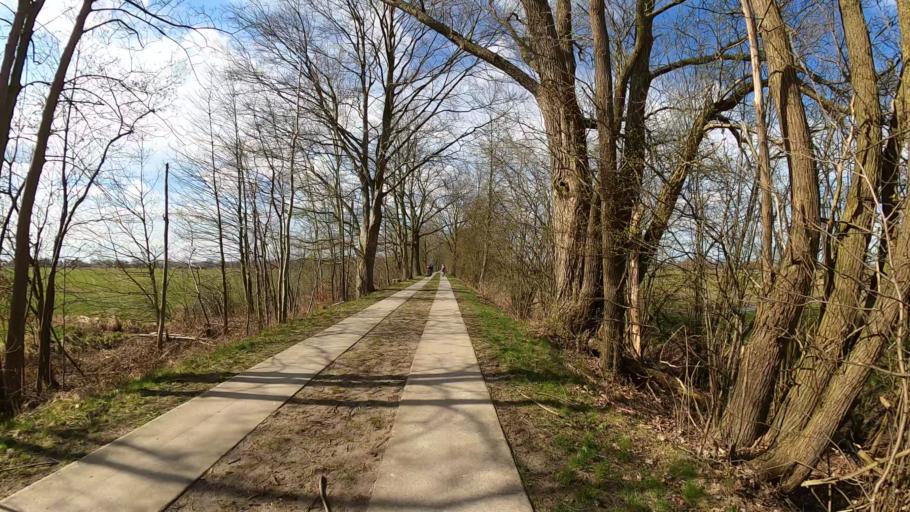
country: DE
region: Lower Saxony
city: Stelle
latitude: 53.4255
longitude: 10.1614
